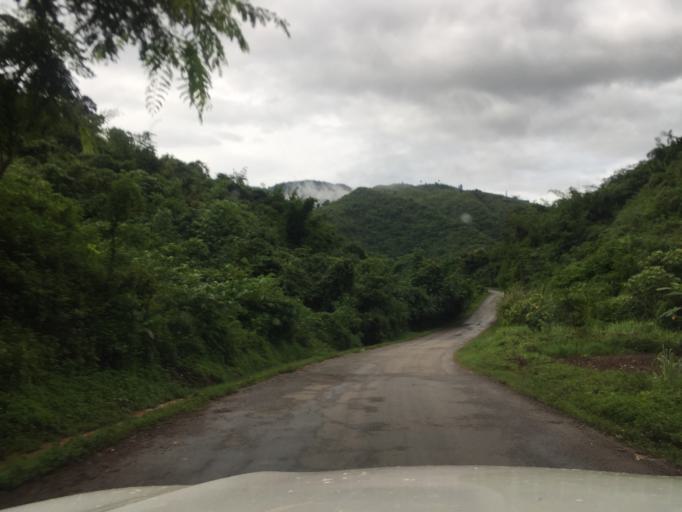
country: LA
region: Oudomxai
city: Muang La
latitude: 20.7950
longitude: 102.0856
